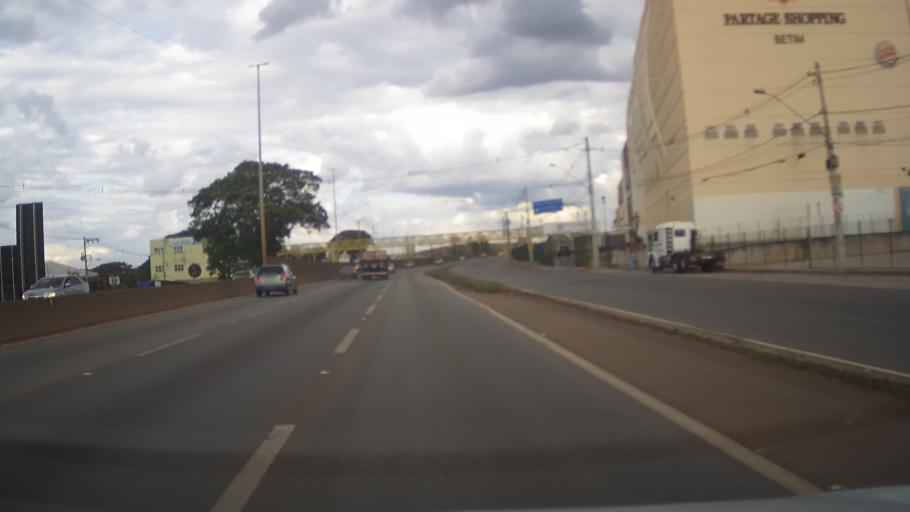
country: BR
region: Minas Gerais
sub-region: Betim
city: Betim
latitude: -19.9620
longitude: -44.1624
